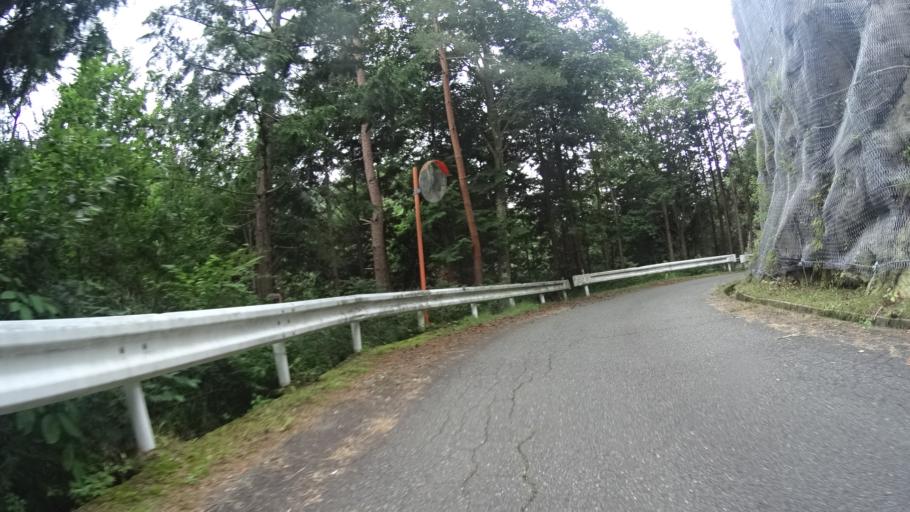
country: JP
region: Yamanashi
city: Kofu-shi
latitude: 35.8124
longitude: 138.5948
